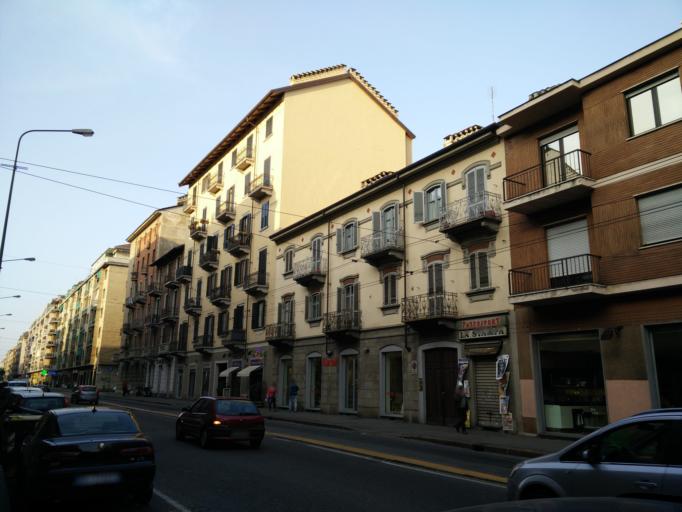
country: IT
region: Piedmont
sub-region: Provincia di Torino
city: Moncalieri
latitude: 45.0289
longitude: 7.6680
